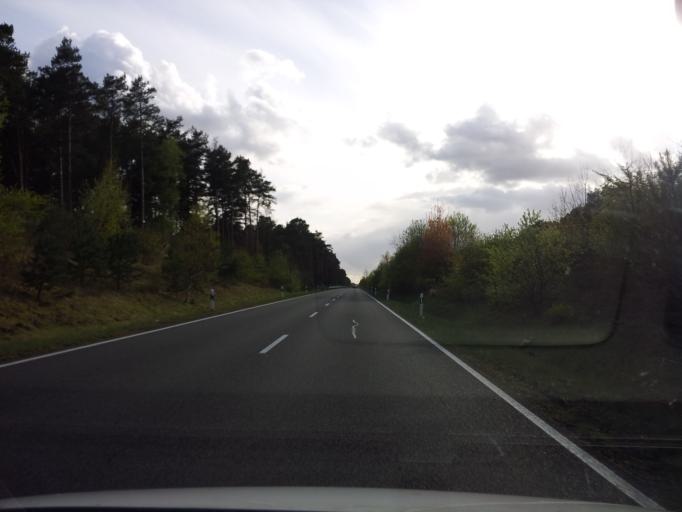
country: DE
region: Brandenburg
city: Schenkendobern
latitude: 51.8958
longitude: 14.5944
